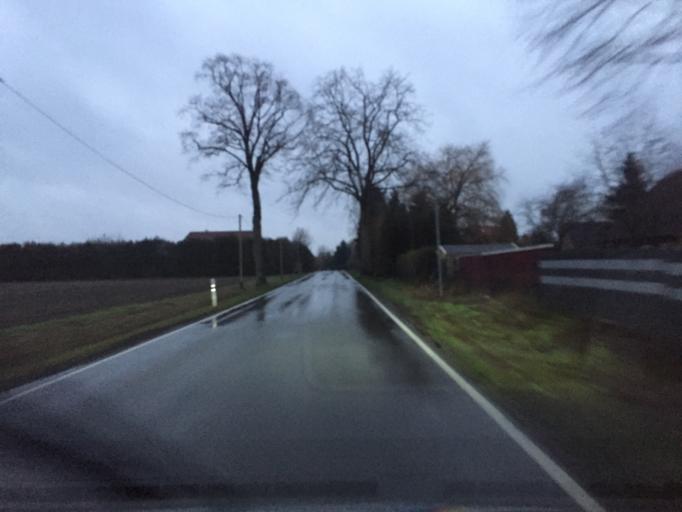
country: DE
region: Lower Saxony
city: Sudwalde
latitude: 52.7929
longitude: 8.8370
